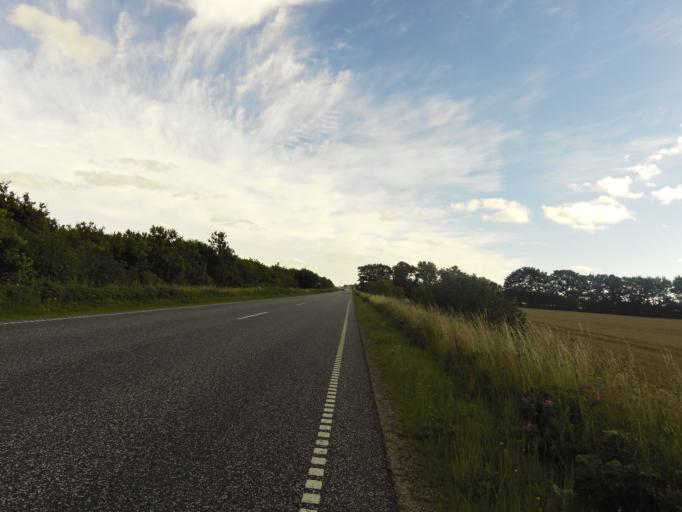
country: DK
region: South Denmark
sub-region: Tonder Kommune
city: Toftlund
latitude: 55.1982
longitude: 9.0515
